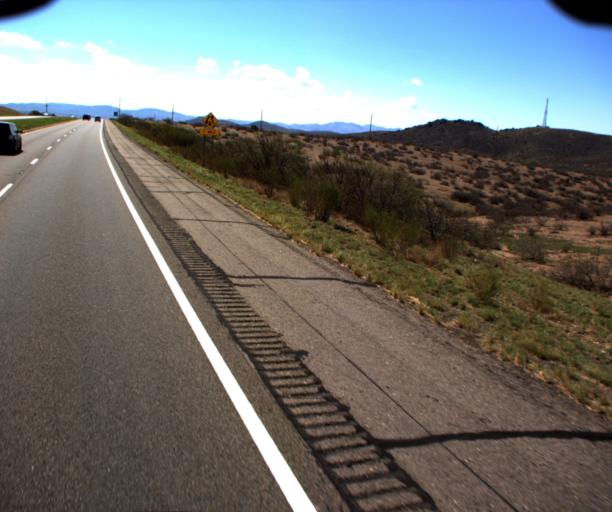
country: US
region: Arizona
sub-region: Yavapai County
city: Spring Valley
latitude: 34.3440
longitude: -112.1406
